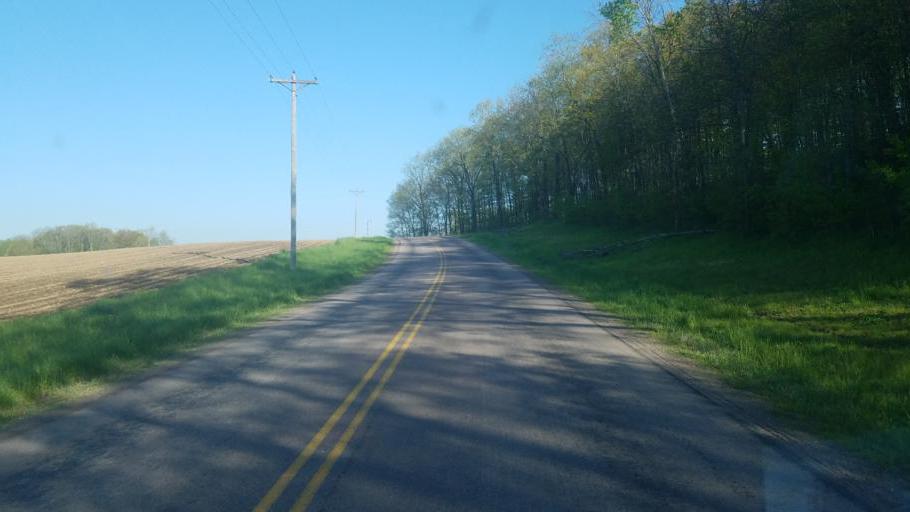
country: US
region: Wisconsin
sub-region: Vernon County
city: Hillsboro
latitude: 43.5897
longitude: -90.3757
